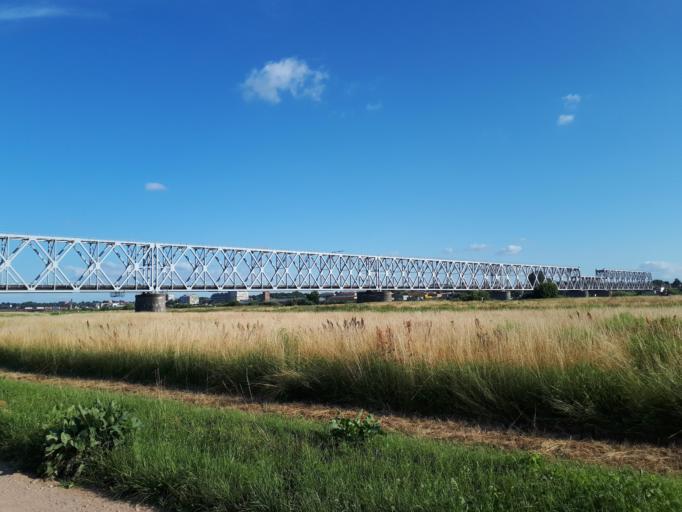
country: RU
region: Kaliningrad
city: Sovetsk
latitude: 55.0941
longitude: 21.8873
